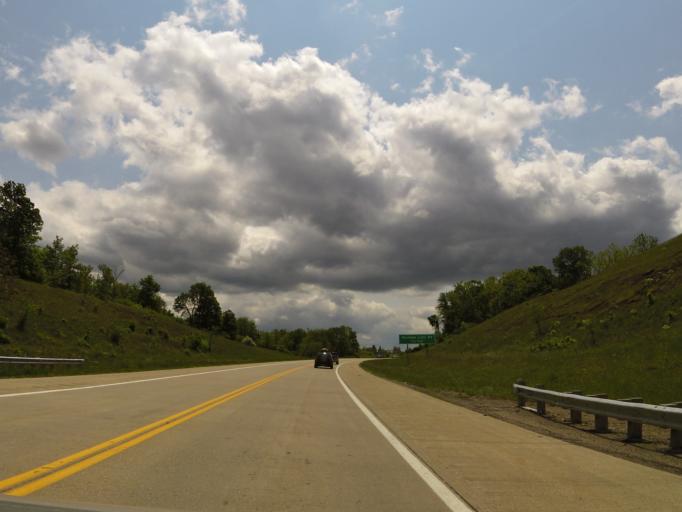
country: US
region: Ohio
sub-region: Athens County
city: Athens
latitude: 39.2066
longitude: -82.0561
